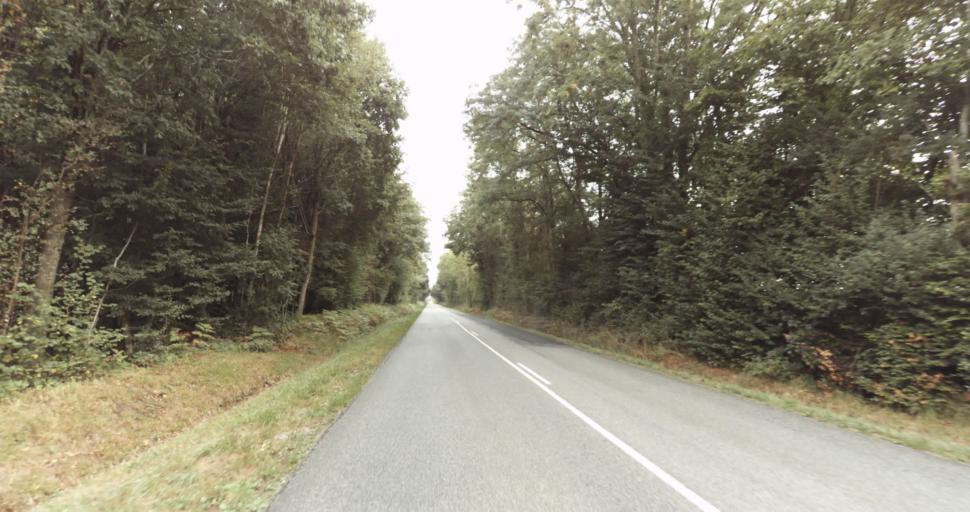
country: FR
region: Lower Normandy
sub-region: Departement de l'Orne
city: Trun
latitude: 48.8848
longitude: 0.0978
